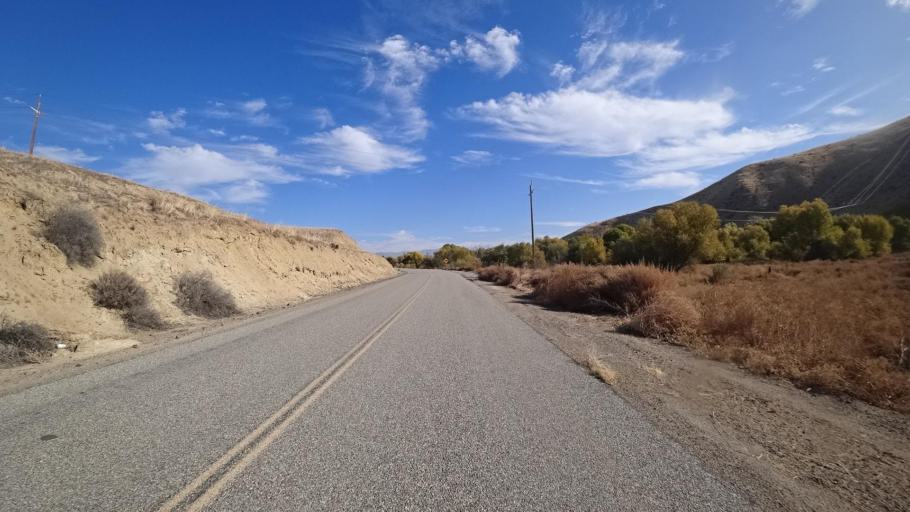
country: US
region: California
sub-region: Kern County
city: Oildale
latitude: 35.5286
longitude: -118.9596
